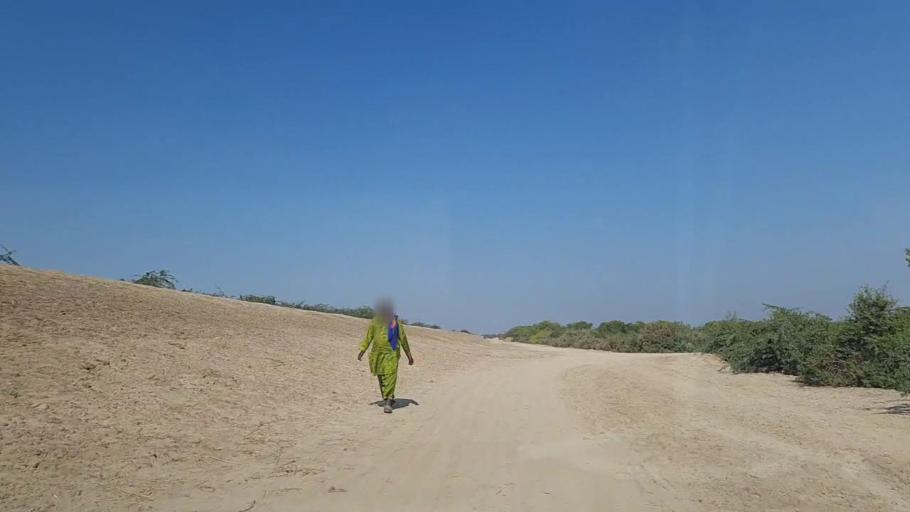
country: PK
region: Sindh
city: Chuhar Jamali
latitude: 24.4735
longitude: 68.0089
